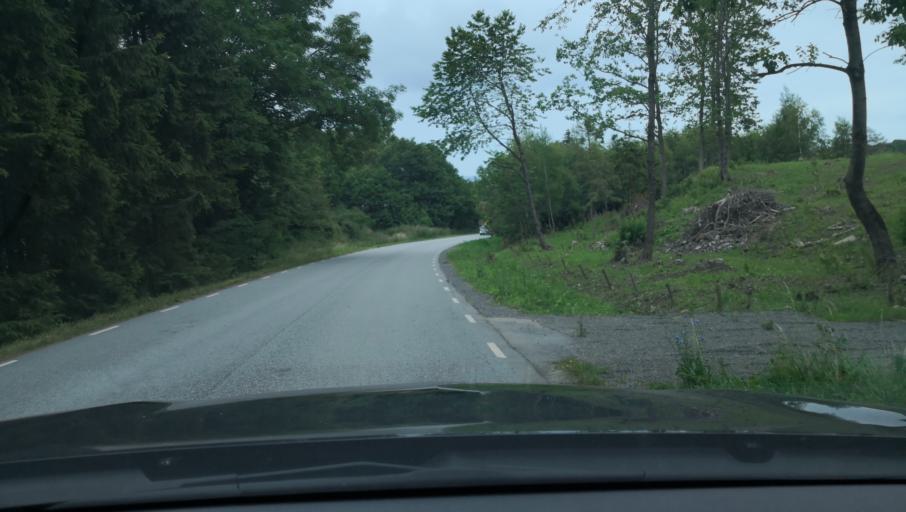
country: SE
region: Skane
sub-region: Simrishamns Kommun
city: Kivik
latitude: 55.6720
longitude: 14.2188
